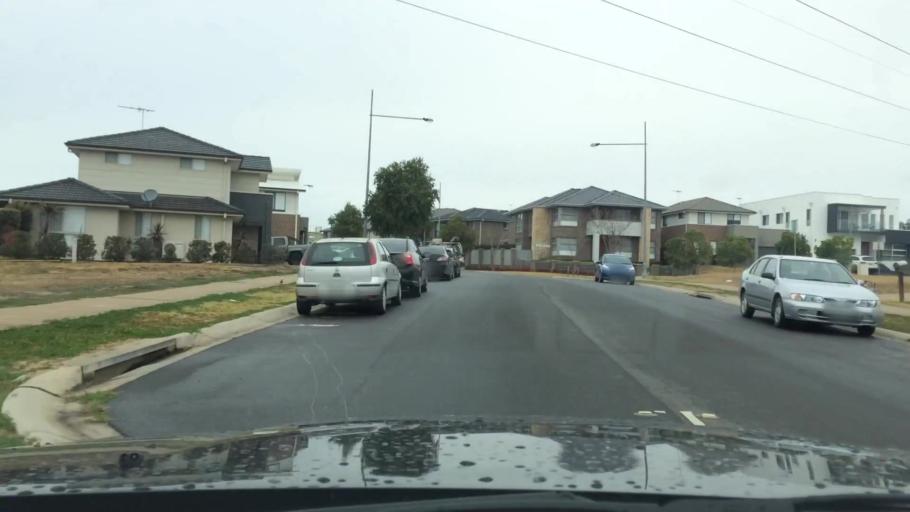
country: AU
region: New South Wales
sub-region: Campbelltown Municipality
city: Denham Court
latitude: -33.9541
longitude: 150.8449
